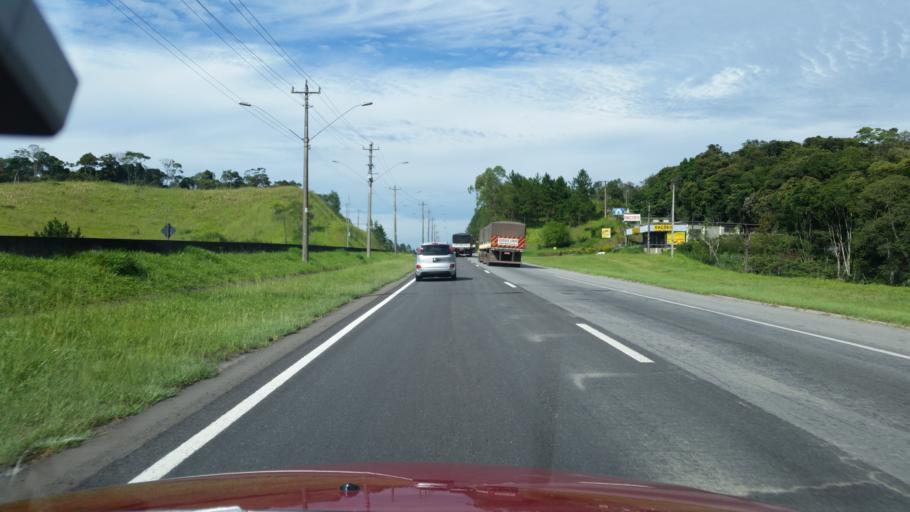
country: BR
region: Sao Paulo
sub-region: Sao Lourenco Da Serra
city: Sao Lourenco da Serra
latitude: -23.8663
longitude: -46.9513
